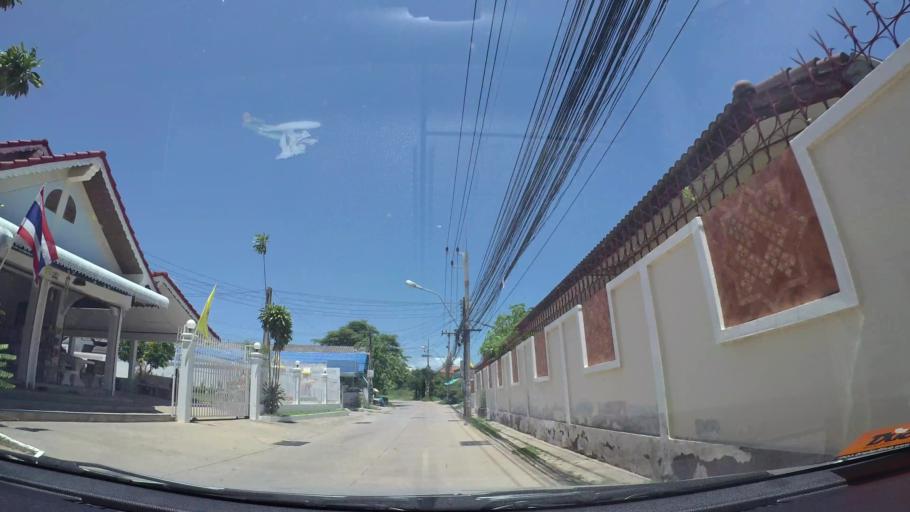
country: TH
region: Chon Buri
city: Phatthaya
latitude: 12.9235
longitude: 100.8963
